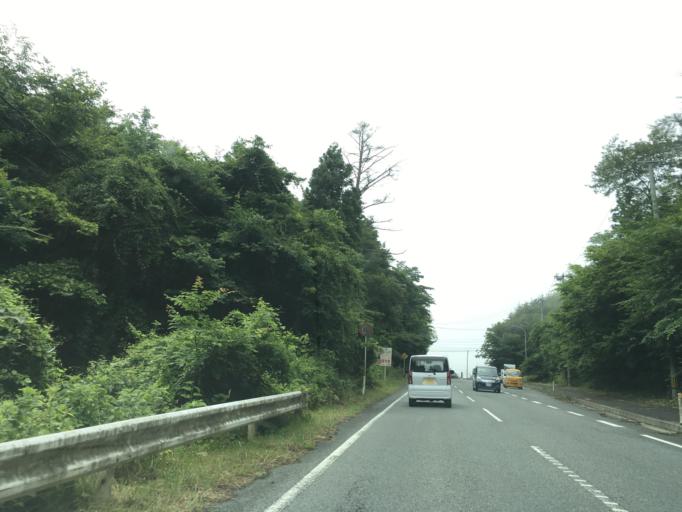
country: JP
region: Iwate
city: Ofunato
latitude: 38.9248
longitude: 141.6404
